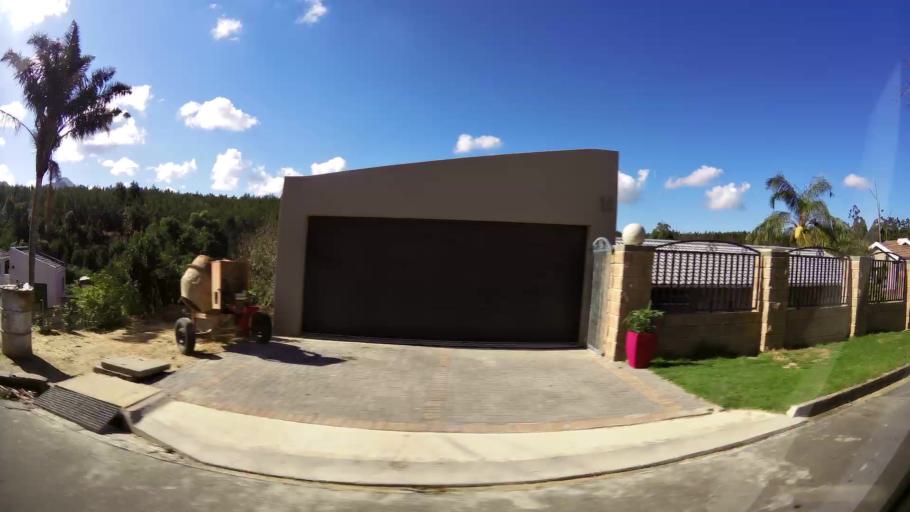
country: ZA
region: Western Cape
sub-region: Eden District Municipality
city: George
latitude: -33.9477
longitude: 22.4809
